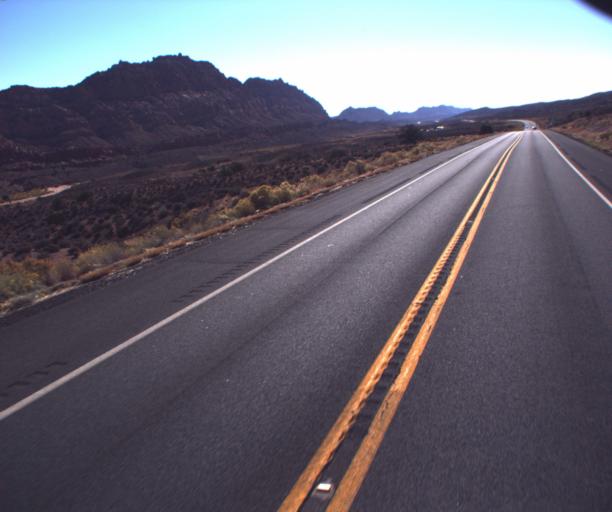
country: US
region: Arizona
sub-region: Coconino County
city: Tuba City
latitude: 36.3410
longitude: -111.4979
